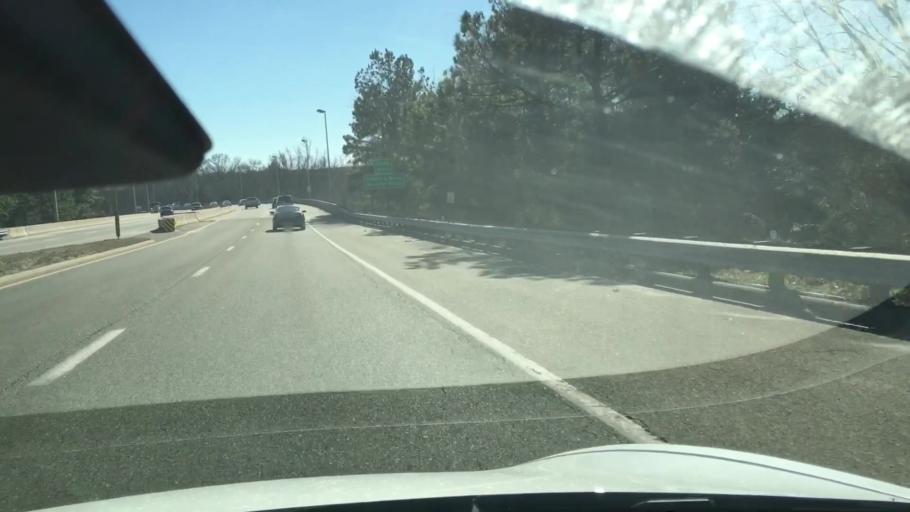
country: US
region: Virginia
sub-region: Henrico County
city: Tuckahoe
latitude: 37.5669
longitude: -77.5775
